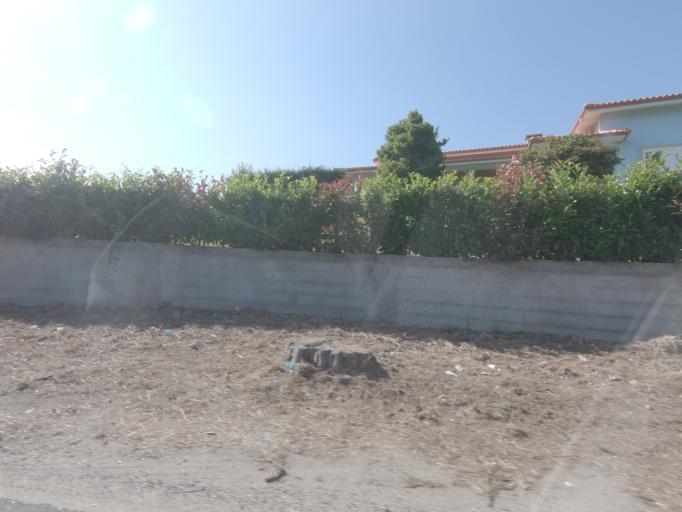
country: PT
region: Vila Real
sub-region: Sabrosa
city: Sabrosa
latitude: 41.2575
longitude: -7.5838
